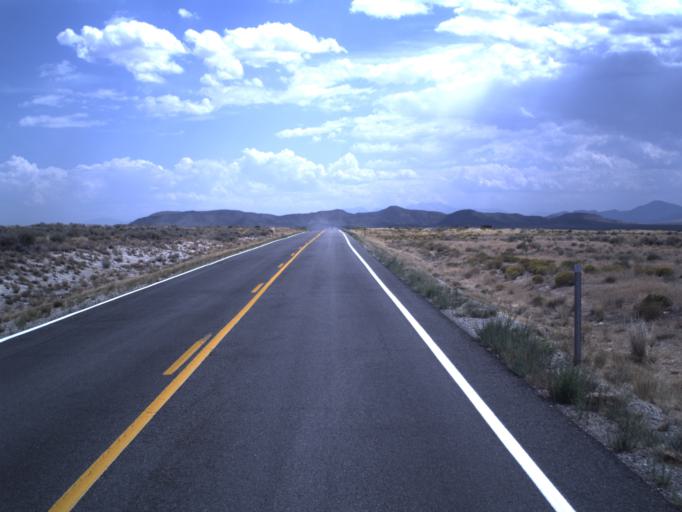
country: US
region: Utah
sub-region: Utah County
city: Eagle Mountain
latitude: 40.2620
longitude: -112.2331
